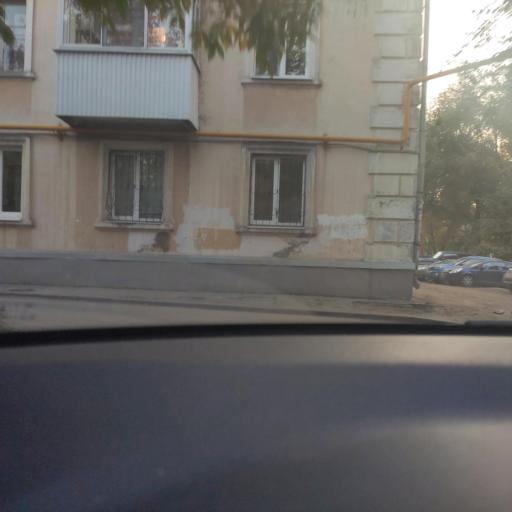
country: RU
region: Samara
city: Samara
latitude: 53.2135
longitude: 50.1556
